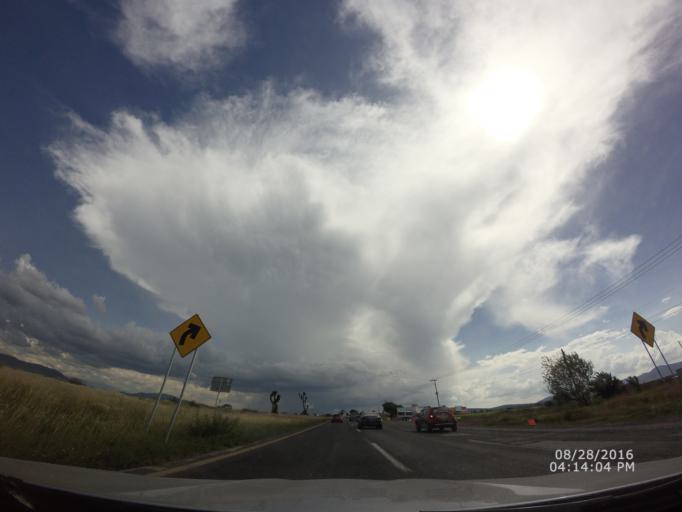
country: MX
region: Hidalgo
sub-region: Zempoala
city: El Mirador
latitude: 20.0131
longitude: -98.8191
